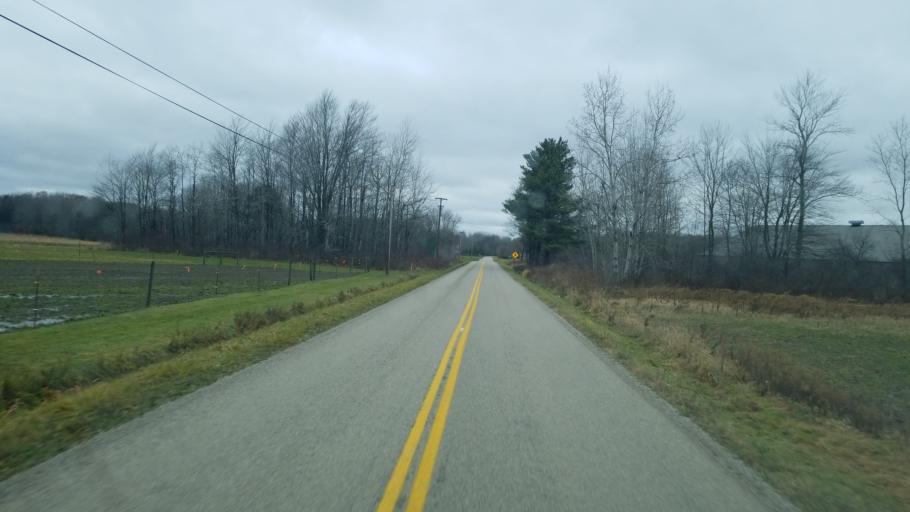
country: US
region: Ohio
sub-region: Ashtabula County
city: Andover
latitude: 41.7125
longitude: -80.6163
